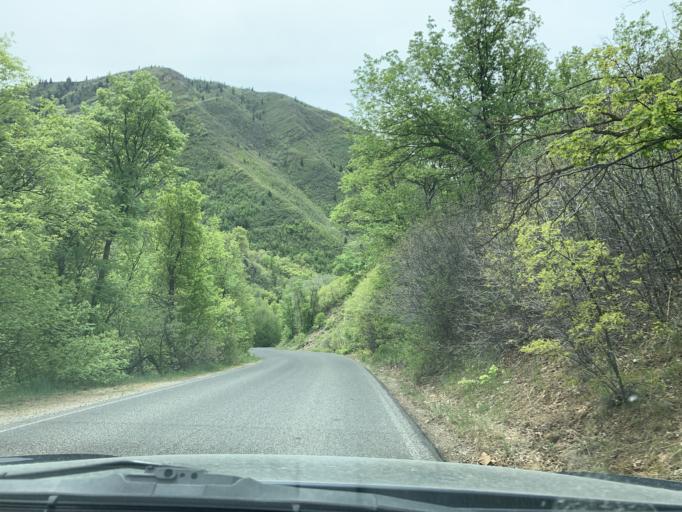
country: US
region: Utah
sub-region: Utah County
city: Mapleton
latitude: 40.1718
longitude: -111.4721
